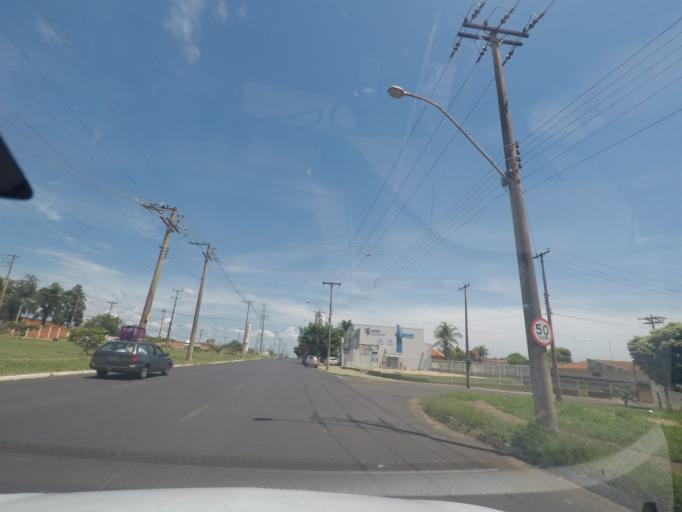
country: BR
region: Sao Paulo
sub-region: Matao
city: Matao
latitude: -21.6145
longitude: -48.3681
